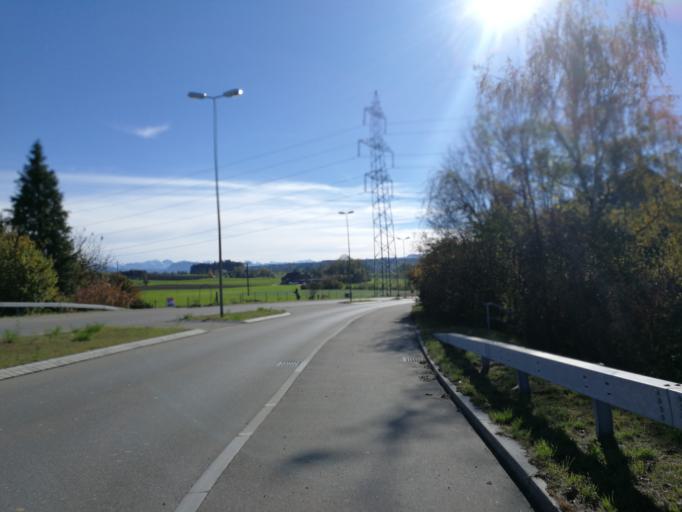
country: CH
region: Zurich
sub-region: Bezirk Uster
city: Moenchaltorf / Dorf
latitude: 47.2881
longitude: 8.7321
